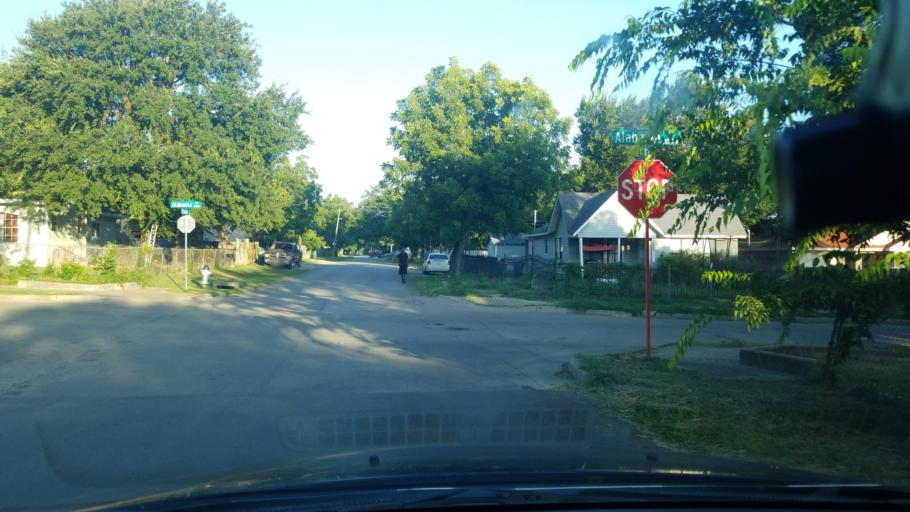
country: US
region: Texas
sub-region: Dallas County
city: Dallas
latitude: 32.7168
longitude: -96.8191
